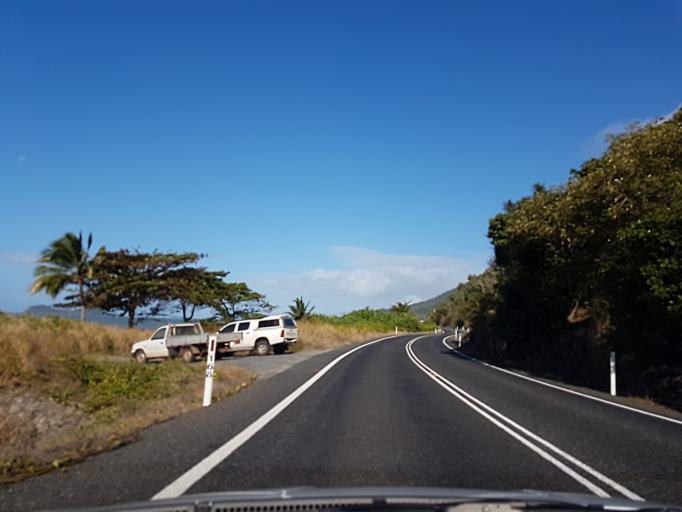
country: AU
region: Queensland
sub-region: Cairns
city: Palm Cove
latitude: -16.7141
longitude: 145.6359
